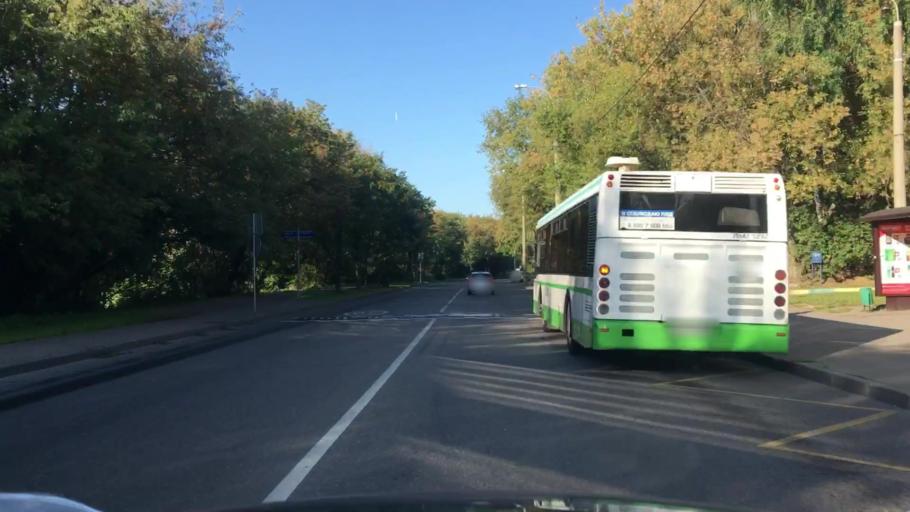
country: RU
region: Moscow
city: Davydkovo
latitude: 55.7222
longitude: 37.4746
